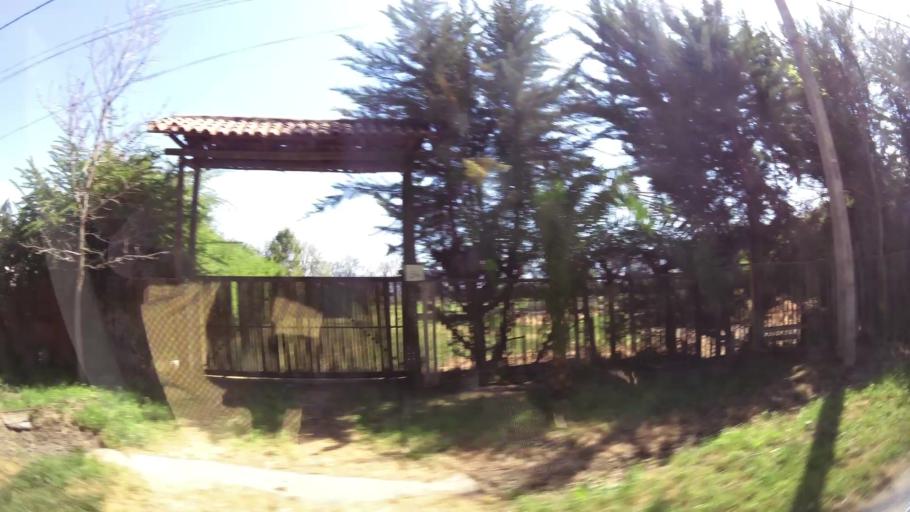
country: CL
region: Santiago Metropolitan
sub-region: Provincia de Talagante
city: Talagante
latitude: -33.6488
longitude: -70.9060
